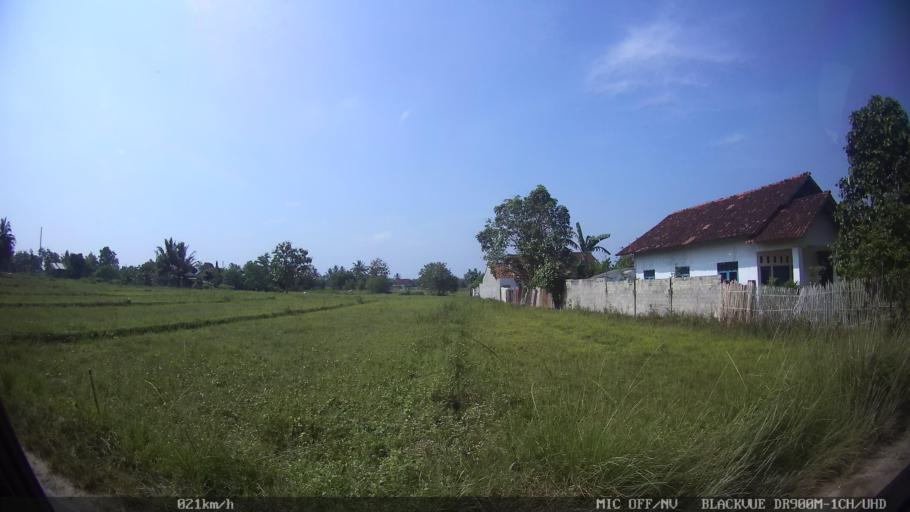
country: ID
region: Lampung
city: Natar
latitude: -5.2648
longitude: 105.2053
